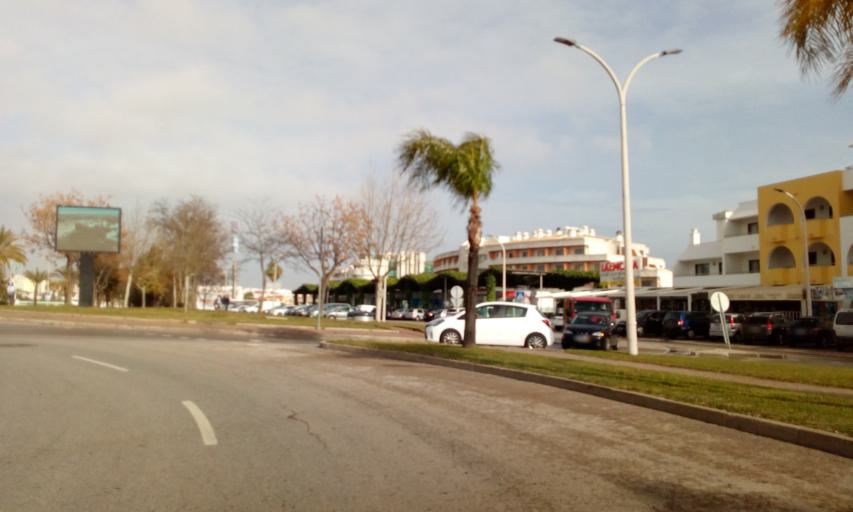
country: PT
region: Faro
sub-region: Albufeira
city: Albufeira
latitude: 37.0917
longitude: -8.2400
